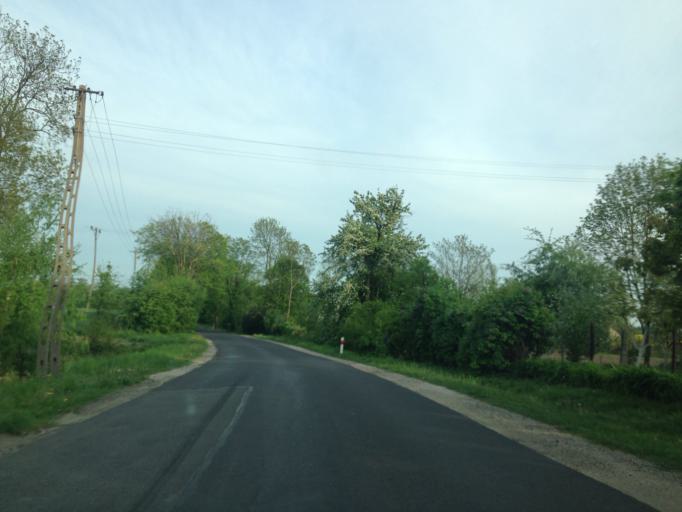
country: PL
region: Kujawsko-Pomorskie
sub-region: Powiat wabrzeski
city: Debowa Laka
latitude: 53.2518
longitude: 19.1196
